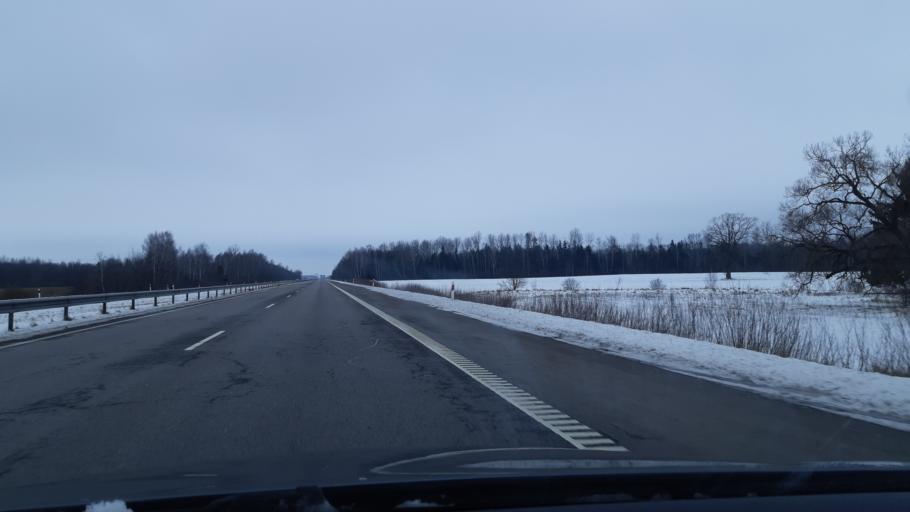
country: LT
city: Vilkija
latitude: 55.1273
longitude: 23.7447
